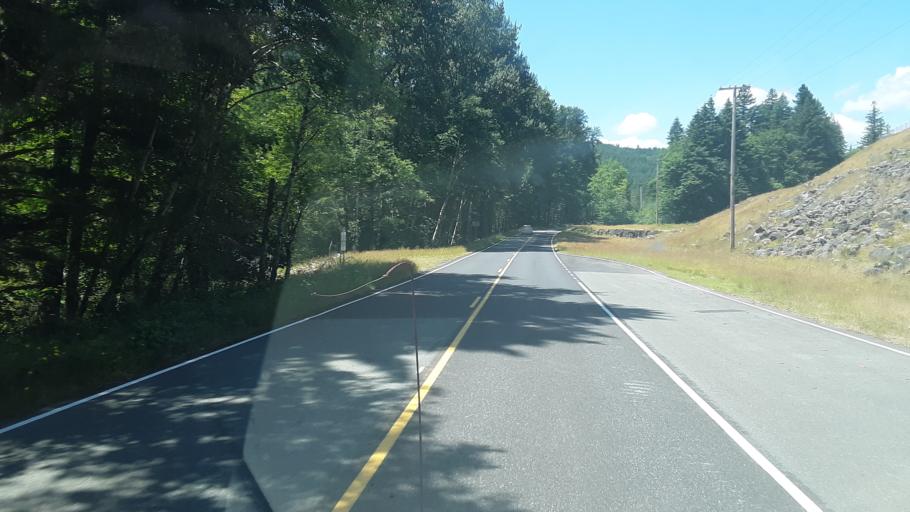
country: US
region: Washington
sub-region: Clark County
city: Yacolt
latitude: 46.0565
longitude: -122.2396
